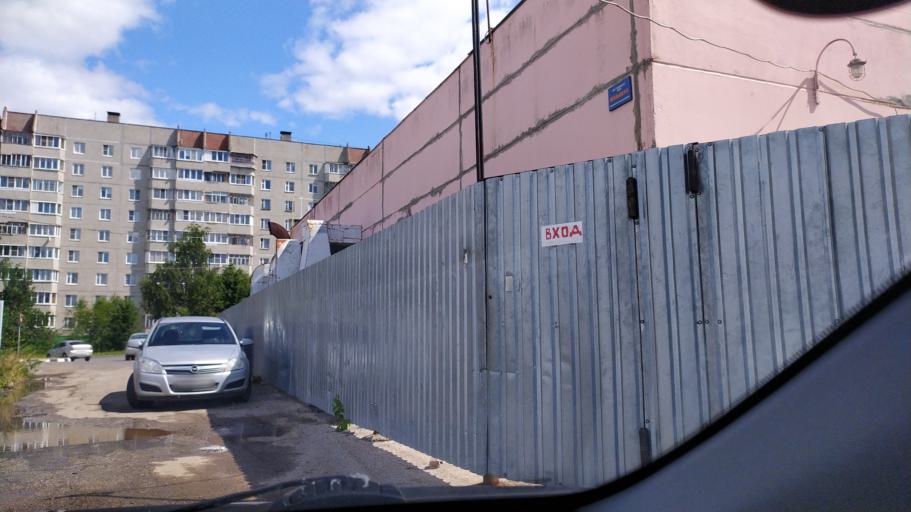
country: RU
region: Chuvashia
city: Novyye Lapsary
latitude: 56.1163
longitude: 47.1757
